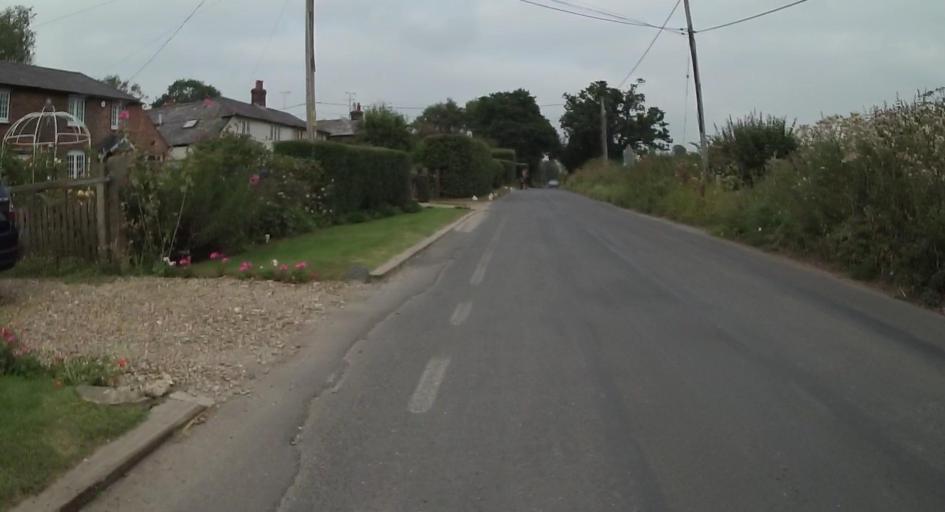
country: GB
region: England
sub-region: Hampshire
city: Old Basing
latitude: 51.2261
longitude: -1.0058
